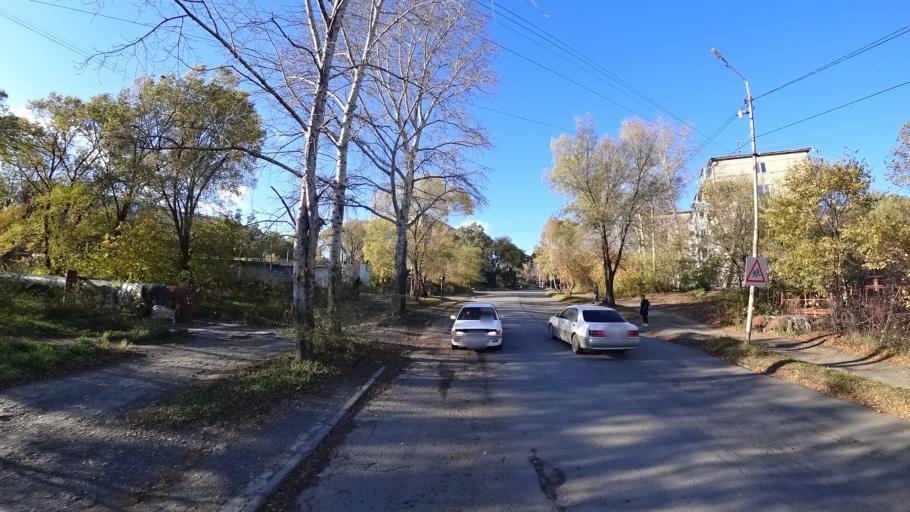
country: RU
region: Khabarovsk Krai
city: Amursk
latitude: 50.2348
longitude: 136.9060
